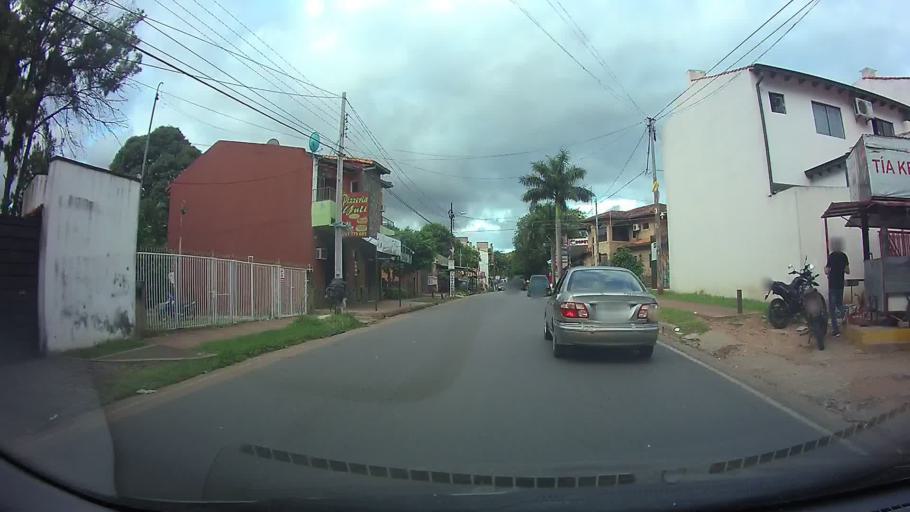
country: PY
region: Central
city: Fernando de la Mora
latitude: -25.3075
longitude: -57.5271
